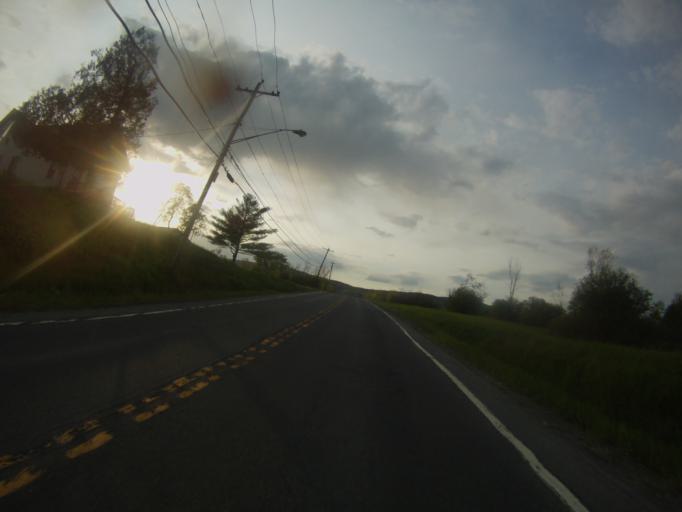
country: US
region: New York
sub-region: Essex County
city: Ticonderoga
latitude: 43.8662
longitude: -73.4375
